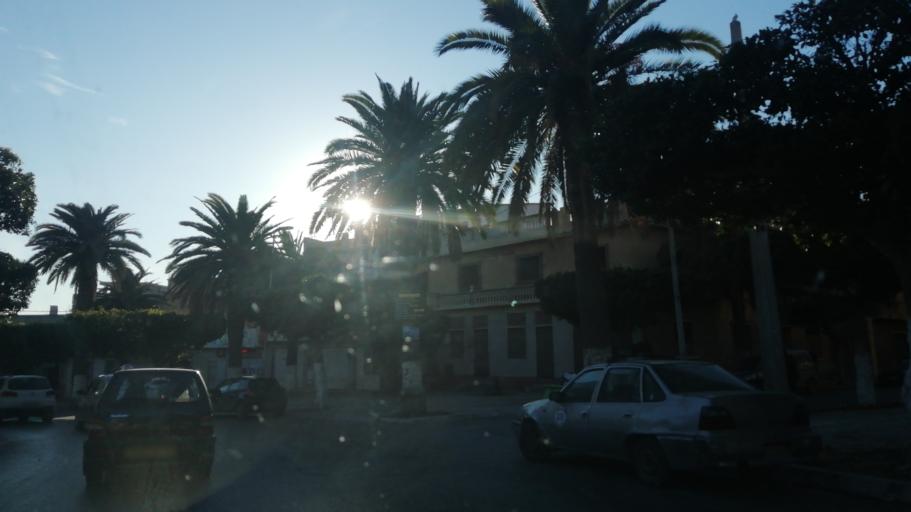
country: DZ
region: Oran
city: Oran
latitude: 35.7118
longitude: -0.6203
